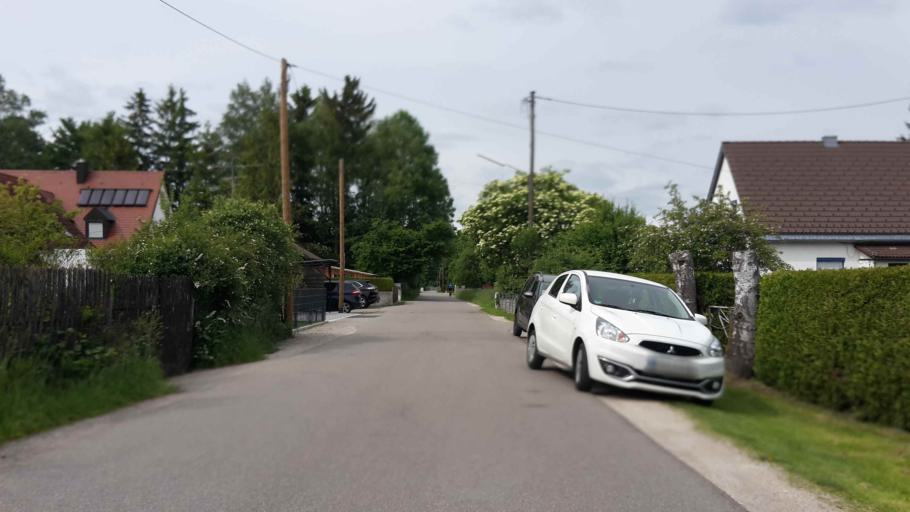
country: DE
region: Bavaria
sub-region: Upper Bavaria
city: Dachau
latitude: 48.2211
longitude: 11.4270
